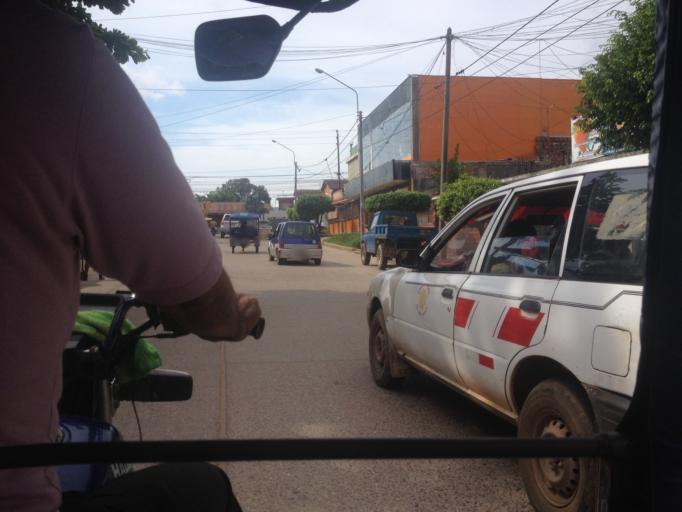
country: PE
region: Ucayali
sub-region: Provincia de Coronel Portillo
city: Pucallpa
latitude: -8.3817
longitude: -74.5361
